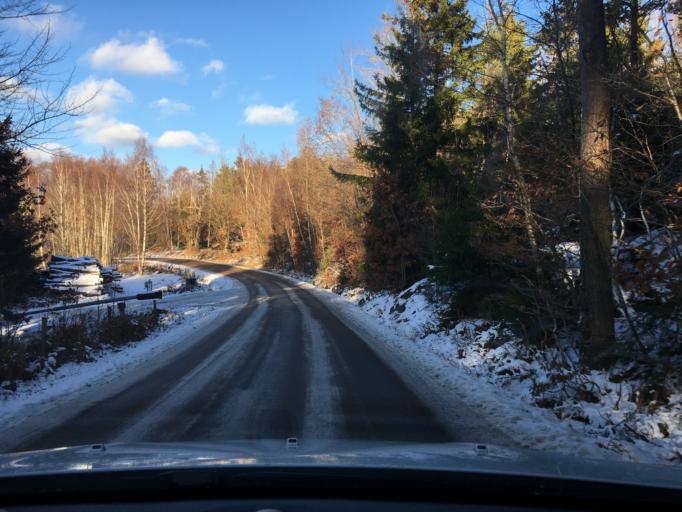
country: SE
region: Vaestra Goetaland
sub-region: Tjorns Kommun
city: Myggenas
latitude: 58.0930
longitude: 11.7463
